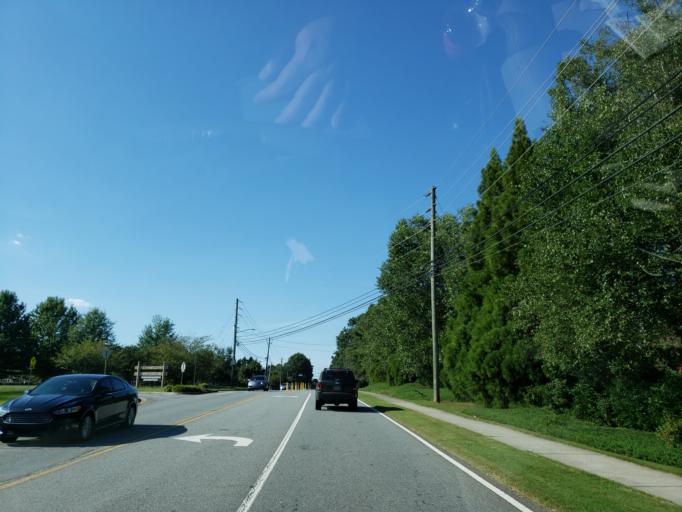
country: US
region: Georgia
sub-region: Fulton County
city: Roswell
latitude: 34.0714
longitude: -84.3605
